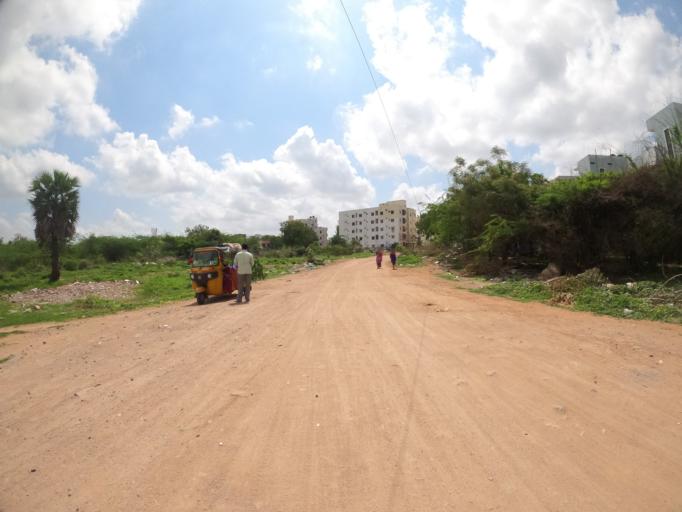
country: IN
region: Telangana
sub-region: Hyderabad
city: Hyderabad
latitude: 17.3627
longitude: 78.3843
